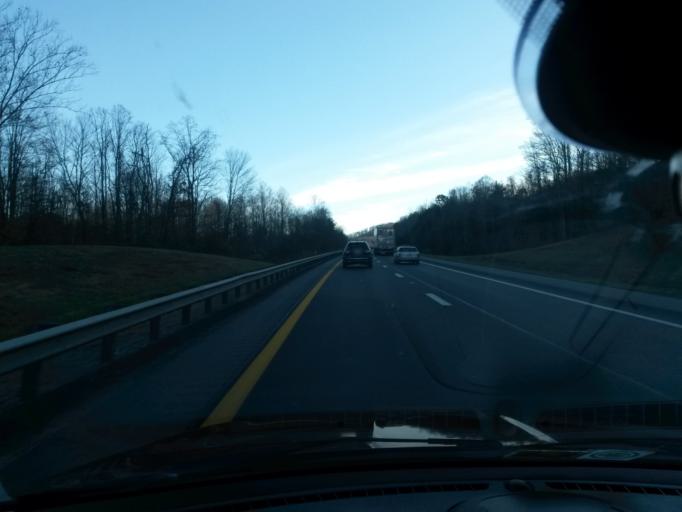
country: US
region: West Virginia
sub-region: Raleigh County
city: Bradley
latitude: 37.8926
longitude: -81.2670
